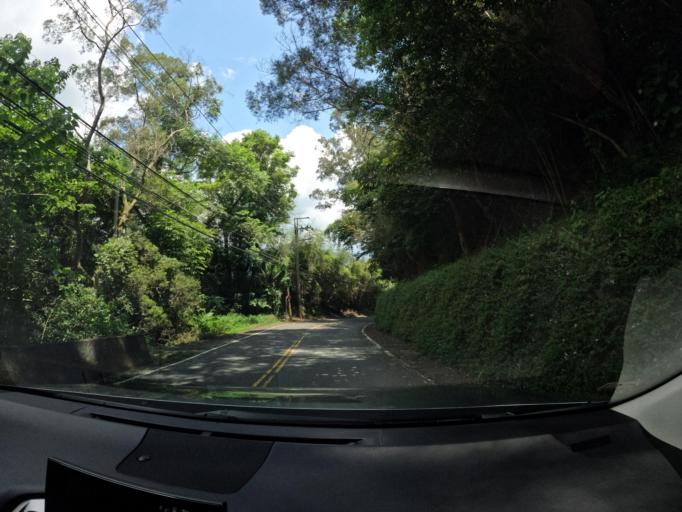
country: TW
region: Taiwan
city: Fengyuan
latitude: 24.3765
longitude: 120.8354
